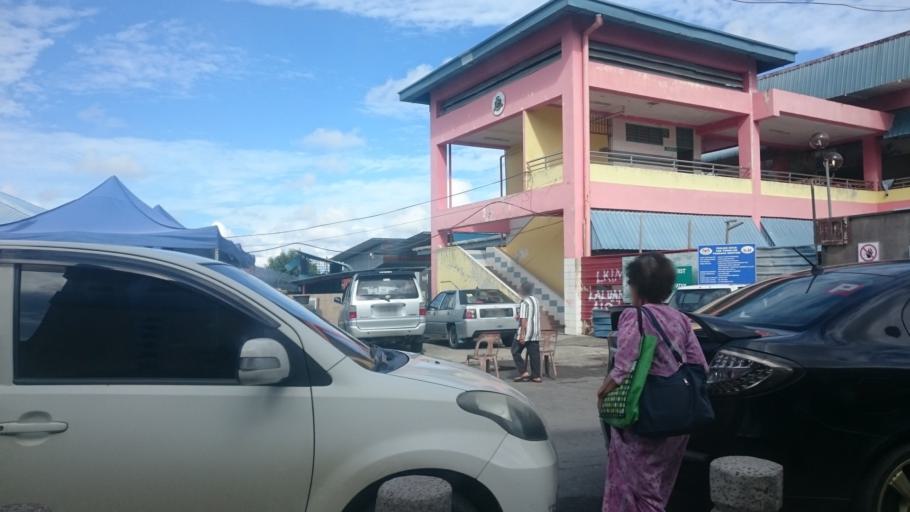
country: MY
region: Sarawak
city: Limbang
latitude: 4.7538
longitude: 115.0089
